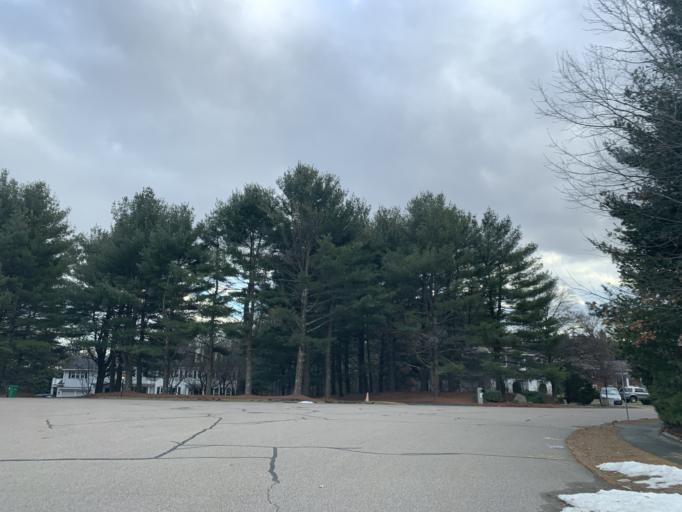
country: US
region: Massachusetts
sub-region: Norfolk County
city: Dedham
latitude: 42.2110
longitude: -71.1577
